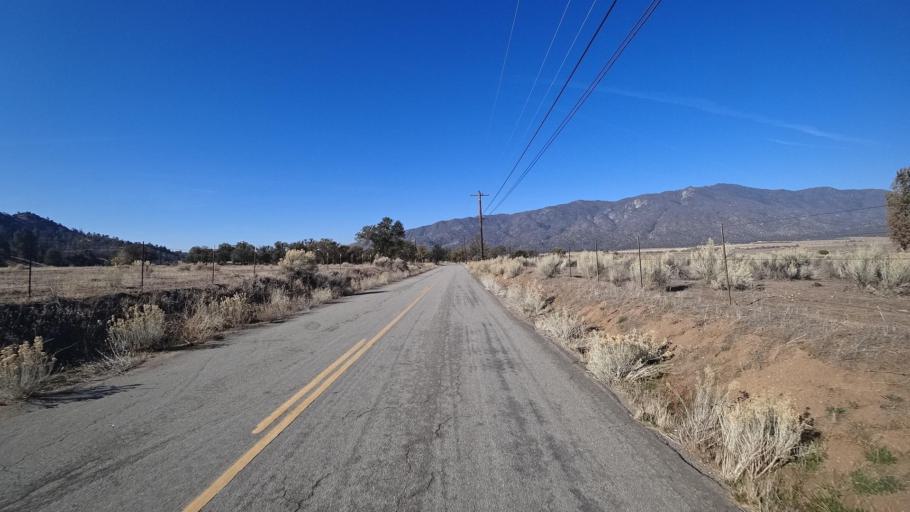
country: US
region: California
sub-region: Kern County
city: Bodfish
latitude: 35.4014
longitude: -118.5124
